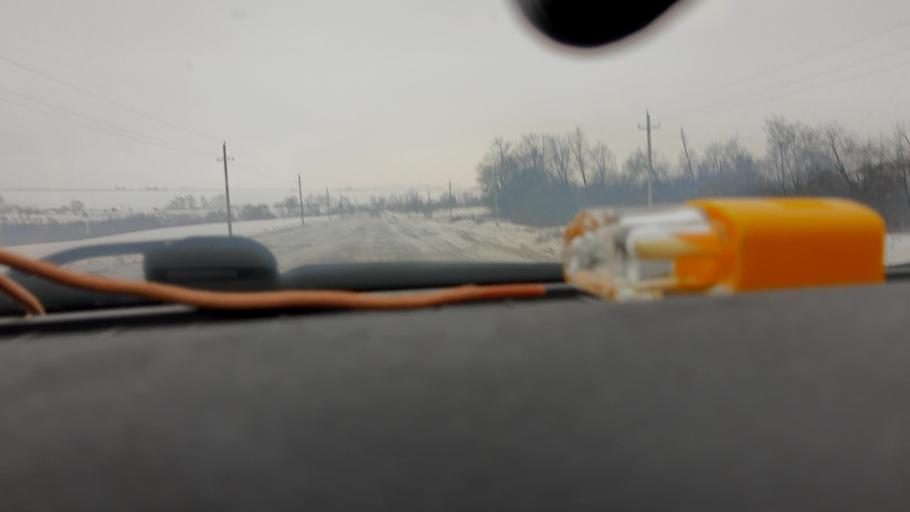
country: RU
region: Bashkortostan
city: Ulukulevo
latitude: 54.5308
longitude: 56.4300
